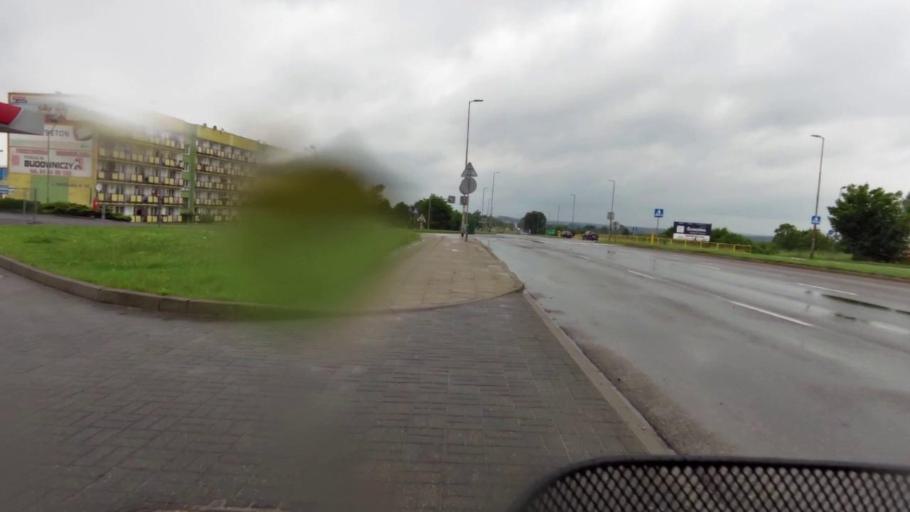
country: PL
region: West Pomeranian Voivodeship
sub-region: Koszalin
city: Koszalin
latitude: 54.2114
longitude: 16.1818
